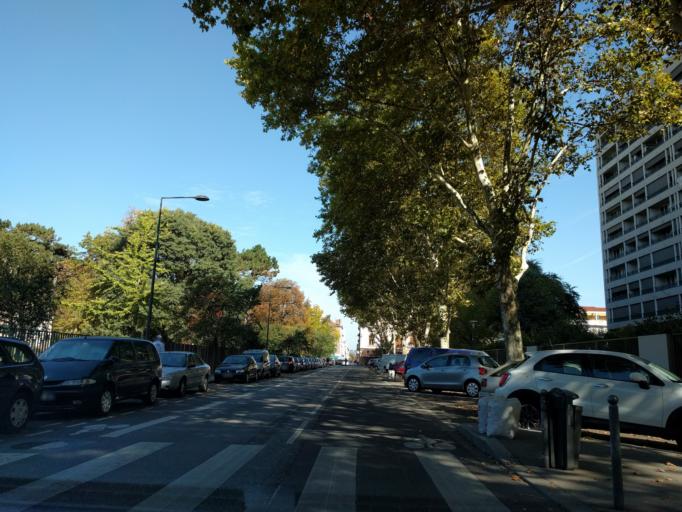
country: FR
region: Rhone-Alpes
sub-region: Departement du Rhone
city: Villeurbanne
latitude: 45.7651
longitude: 4.8895
